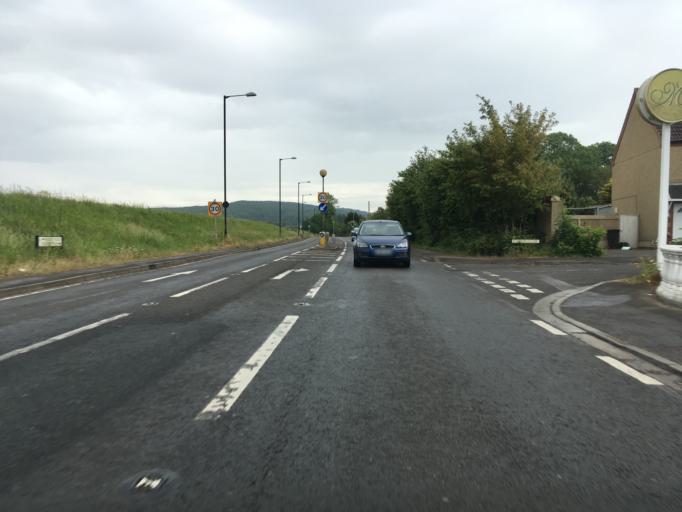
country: GB
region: England
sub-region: North Somerset
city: Congresbury
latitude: 51.3718
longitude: -2.8197
